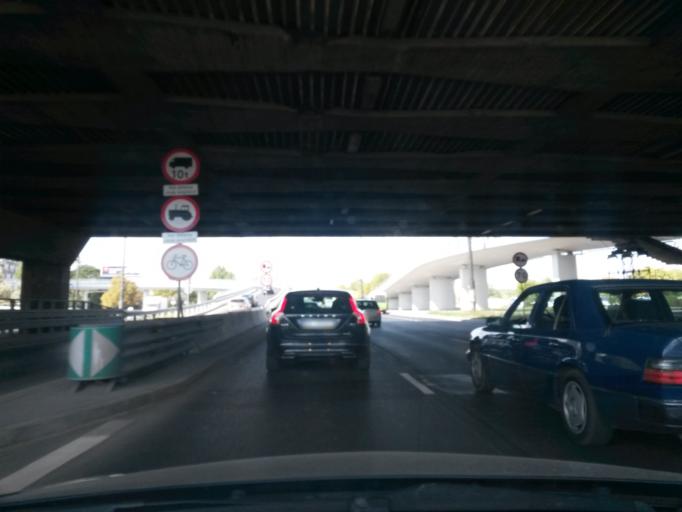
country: PL
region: Masovian Voivodeship
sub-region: Warszawa
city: Srodmiescie
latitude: 52.2241
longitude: 21.0440
